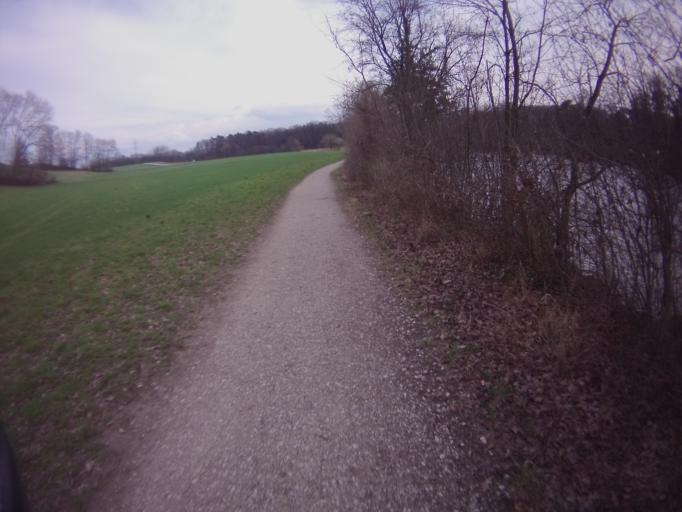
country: CH
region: Aargau
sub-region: Bezirk Baden
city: Wurenlos
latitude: 47.4336
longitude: 8.3748
